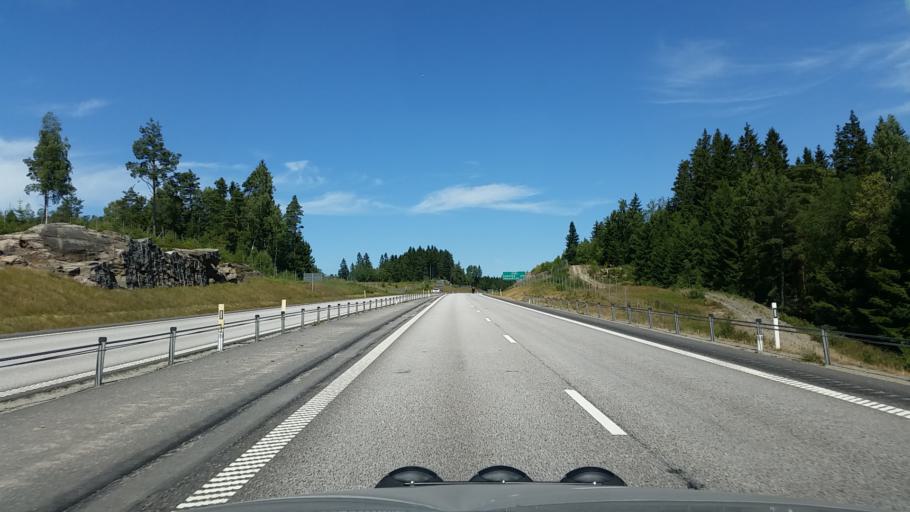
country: SE
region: Vaestra Goetaland
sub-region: Lilla Edets Kommun
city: Lodose
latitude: 58.0469
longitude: 12.1725
